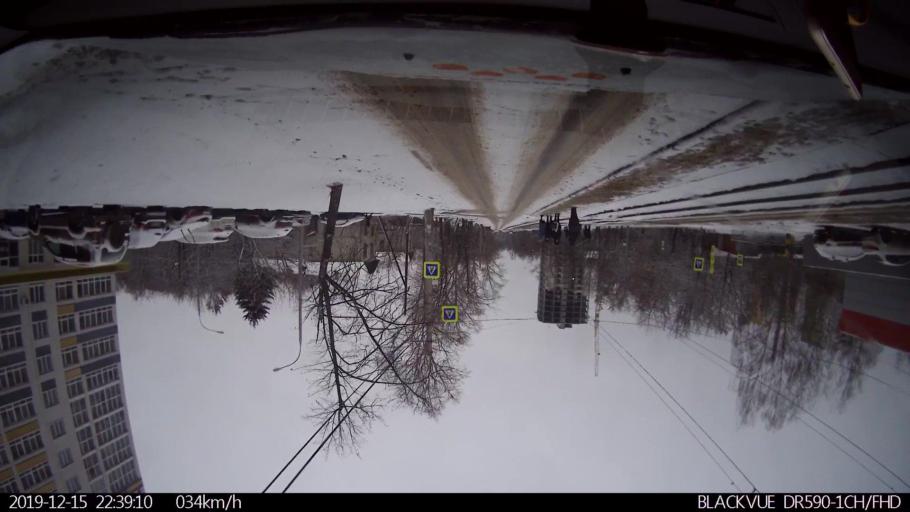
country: RU
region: Nizjnij Novgorod
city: Gorbatovka
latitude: 56.3406
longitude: 43.8389
